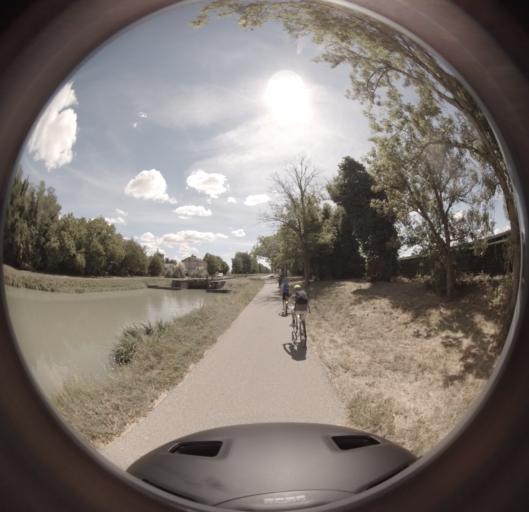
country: FR
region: Midi-Pyrenees
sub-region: Departement du Tarn-et-Garonne
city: Castelsarrasin
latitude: 44.0634
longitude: 1.1023
